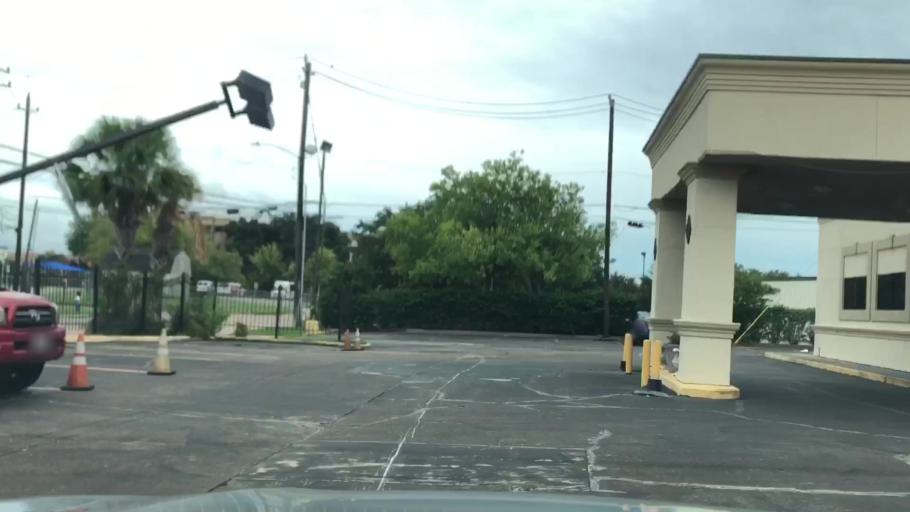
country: US
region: Texas
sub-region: Harris County
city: Bellaire
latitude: 29.7175
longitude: -95.4963
